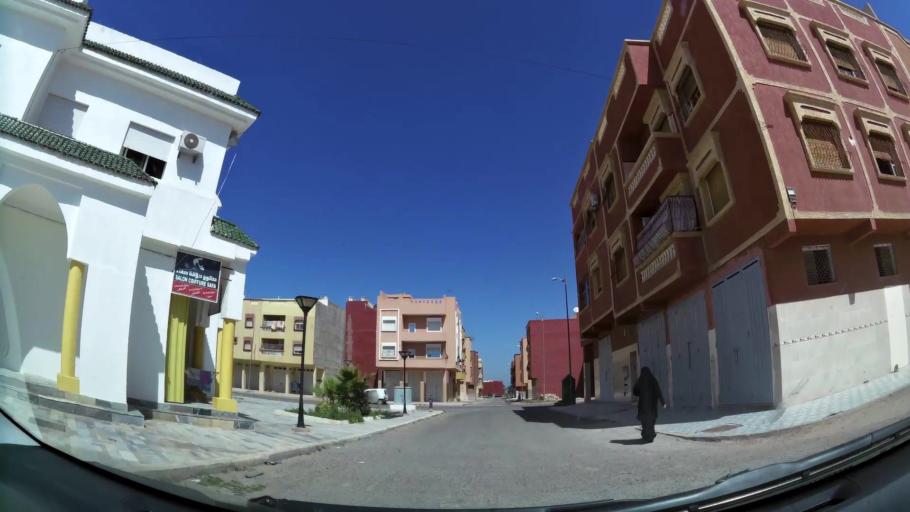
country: MA
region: Souss-Massa-Draa
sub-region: Inezgane-Ait Mellou
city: Inezgane
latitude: 30.3304
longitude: -9.5093
